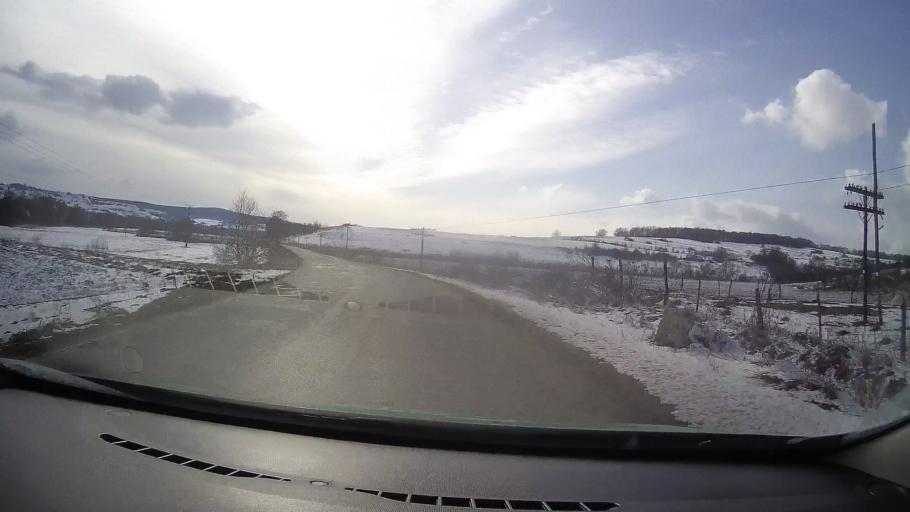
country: RO
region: Sibiu
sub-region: Comuna Iacobeni
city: Iacobeni
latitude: 46.0499
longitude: 24.7663
